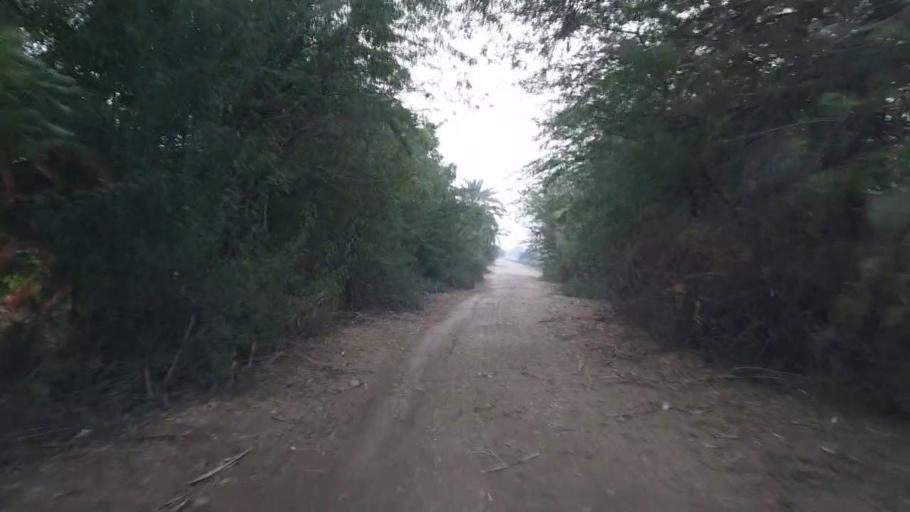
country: PK
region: Sindh
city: Karaundi
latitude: 26.9541
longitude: 68.4548
